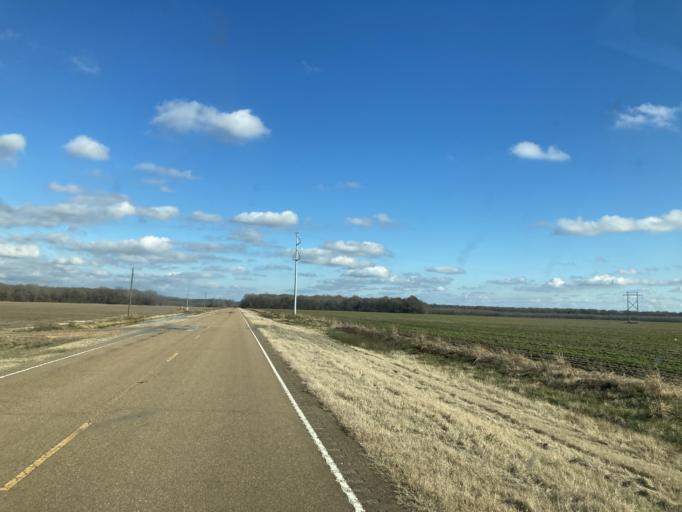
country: US
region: Mississippi
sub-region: Yazoo County
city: Yazoo City
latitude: 32.9626
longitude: -90.4875
